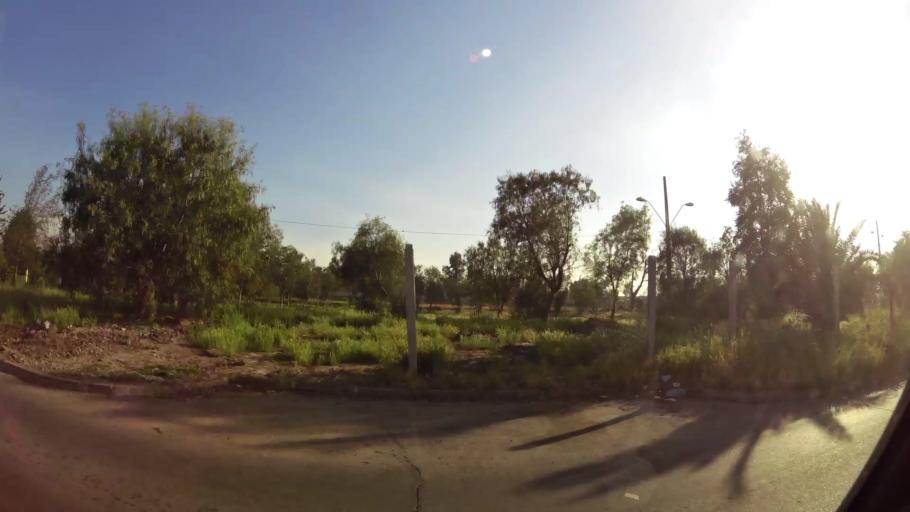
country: CL
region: Santiago Metropolitan
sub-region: Provincia de Santiago
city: Lo Prado
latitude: -33.4494
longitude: -70.7646
